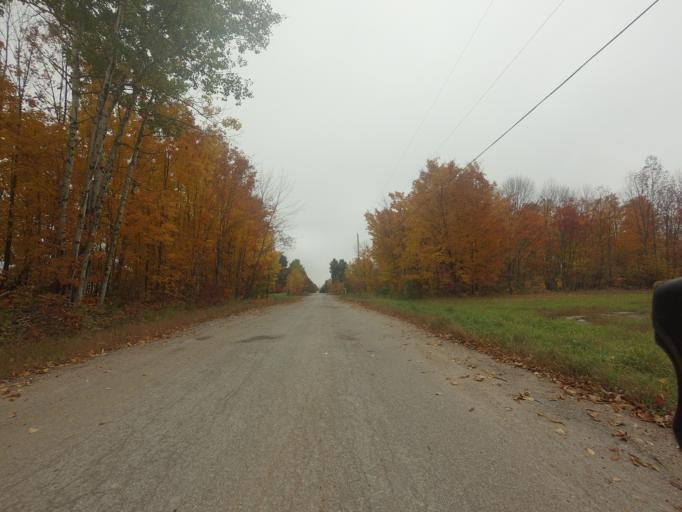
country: CA
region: Ontario
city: Petawawa
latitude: 45.7537
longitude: -77.2618
